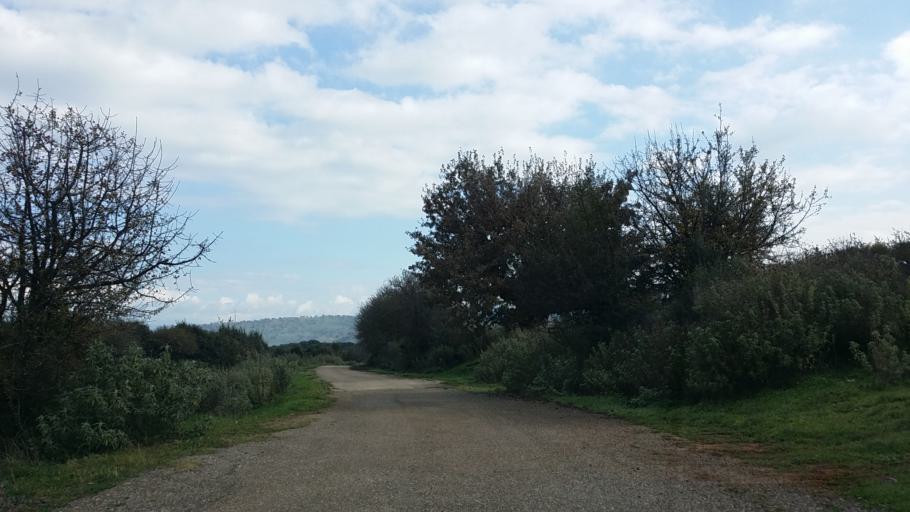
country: GR
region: West Greece
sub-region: Nomos Aitolias kai Akarnanias
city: Katouna
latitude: 38.8584
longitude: 21.0624
